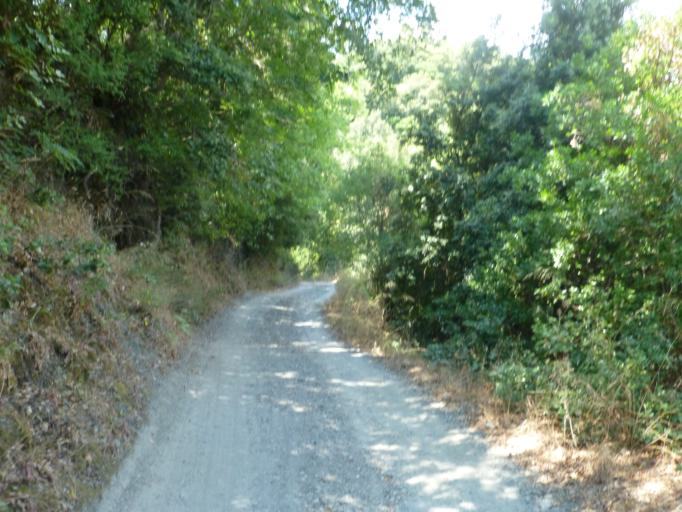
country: IT
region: Calabria
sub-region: Provincia di Reggio Calabria
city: Pazzano
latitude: 38.4804
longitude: 16.4462
